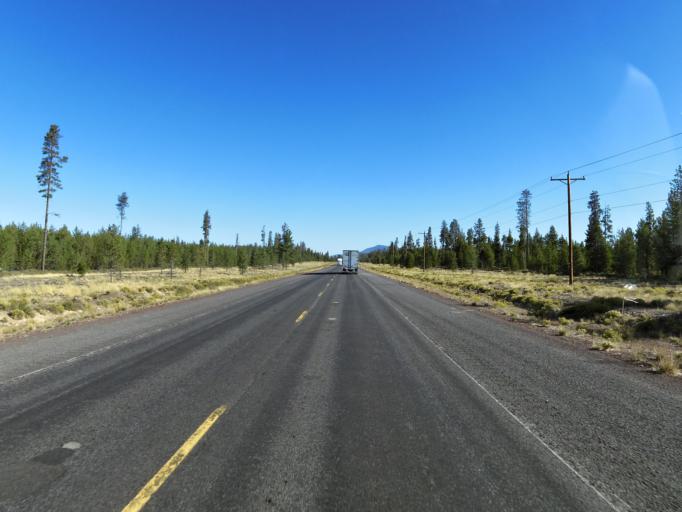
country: US
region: Oregon
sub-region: Deschutes County
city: La Pine
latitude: 43.1633
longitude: -121.7909
